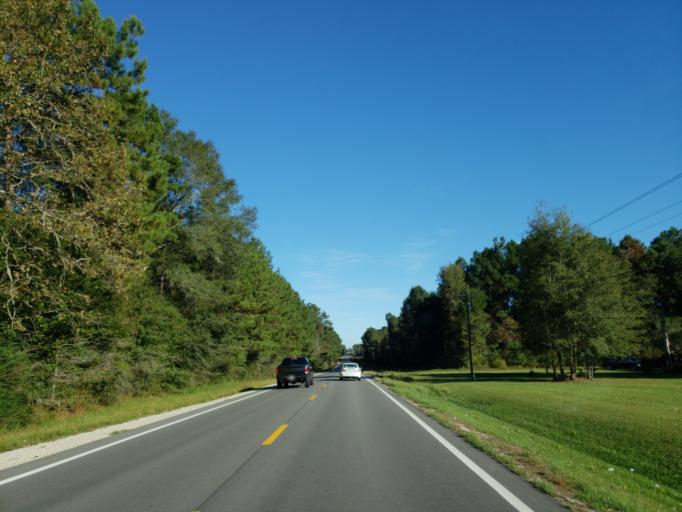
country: US
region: Mississippi
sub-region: Perry County
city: Richton
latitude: 31.3663
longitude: -89.0596
